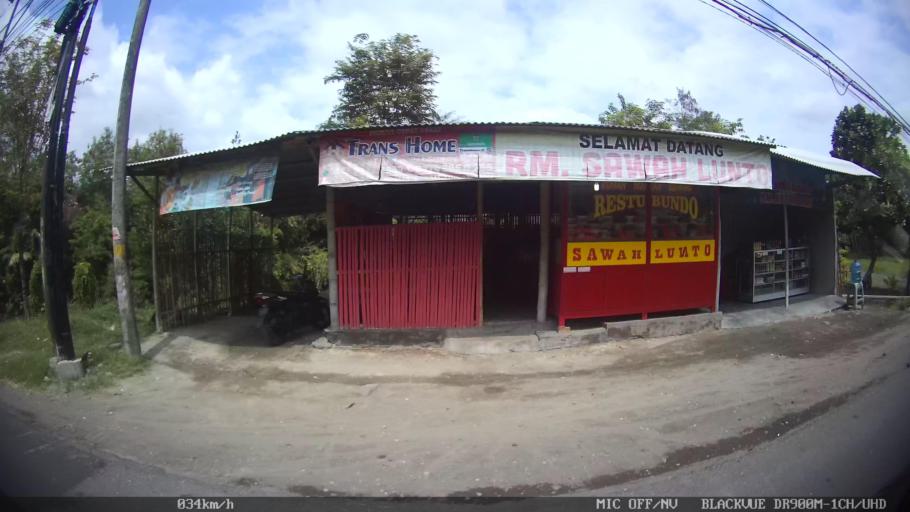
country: ID
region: Central Java
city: Candi Prambanan
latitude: -7.7764
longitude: 110.4736
